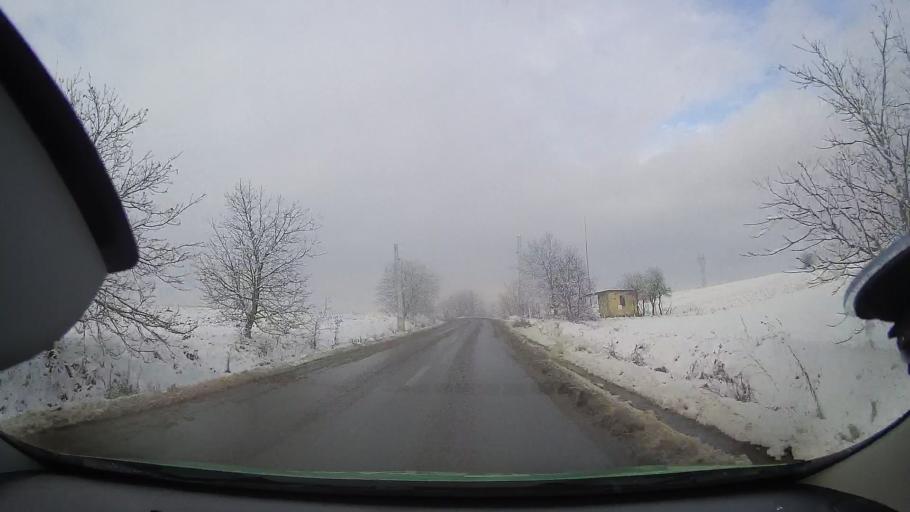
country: RO
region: Mures
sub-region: Comuna Atintis
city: Atintis
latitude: 46.4381
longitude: 24.0935
